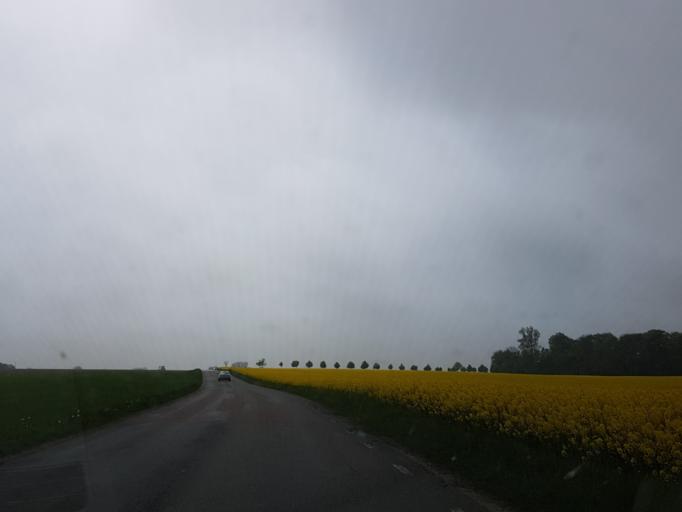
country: SE
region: Skane
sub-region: Tomelilla Kommun
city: Tomelilla
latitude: 55.4705
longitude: 14.0976
